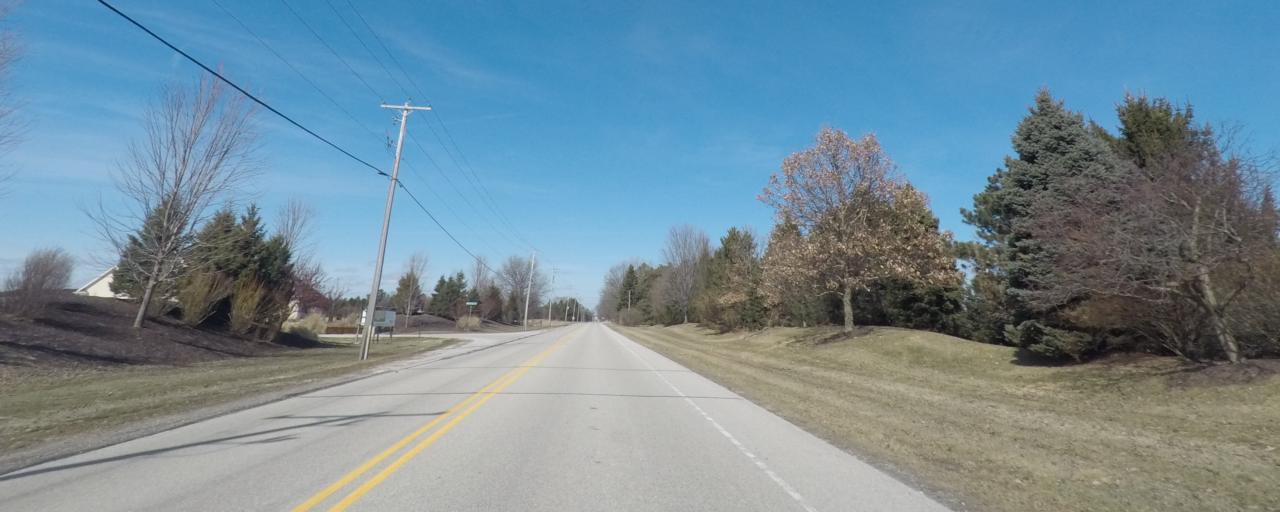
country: US
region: Wisconsin
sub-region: Waukesha County
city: Merton
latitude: 43.1327
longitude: -88.3274
